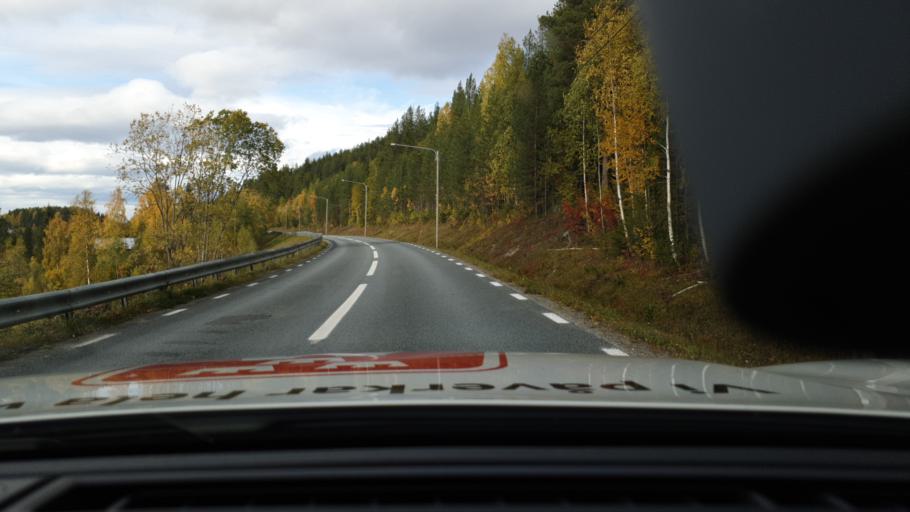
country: SE
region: Vaesterbotten
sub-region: Lycksele Kommun
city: Soderfors
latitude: 65.1018
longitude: 18.3114
